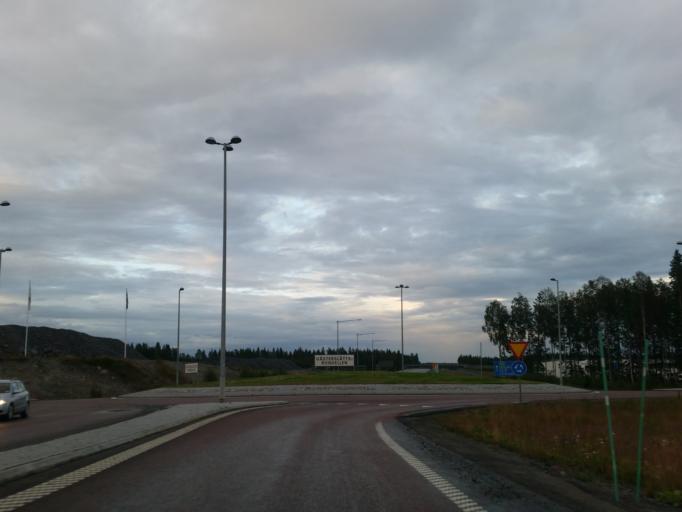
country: SE
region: Vaesterbotten
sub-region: Umea Kommun
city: Roback
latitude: 63.8570
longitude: 20.2062
